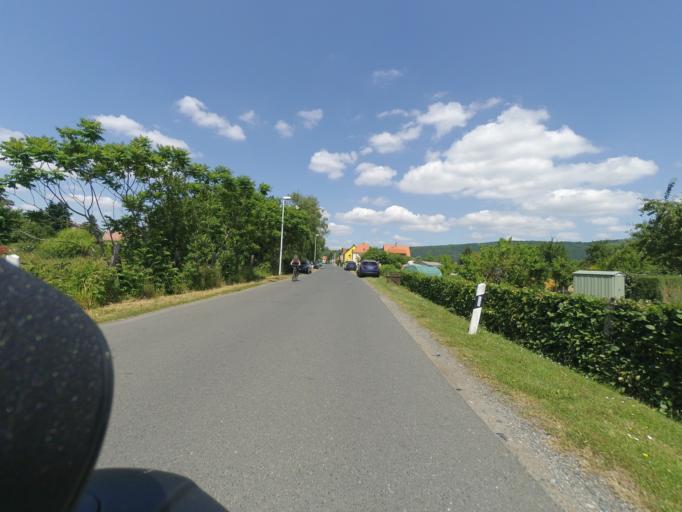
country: DE
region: Saxony
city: Heidenau
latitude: 50.9918
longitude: 13.8830
